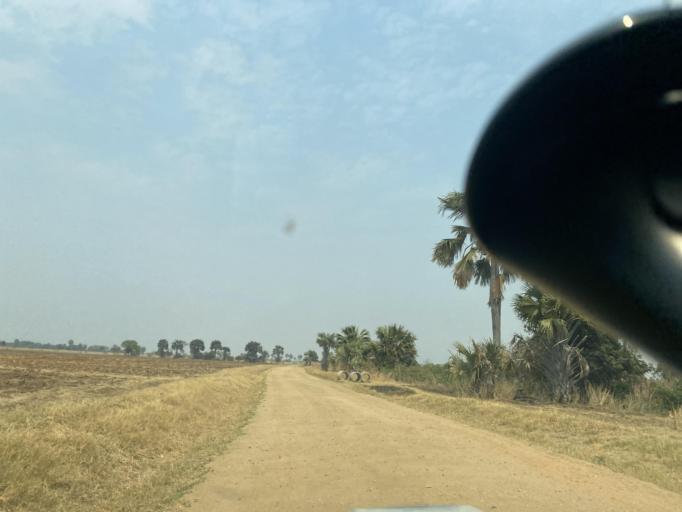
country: ZM
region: Lusaka
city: Kafue
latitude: -15.6468
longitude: 28.0730
